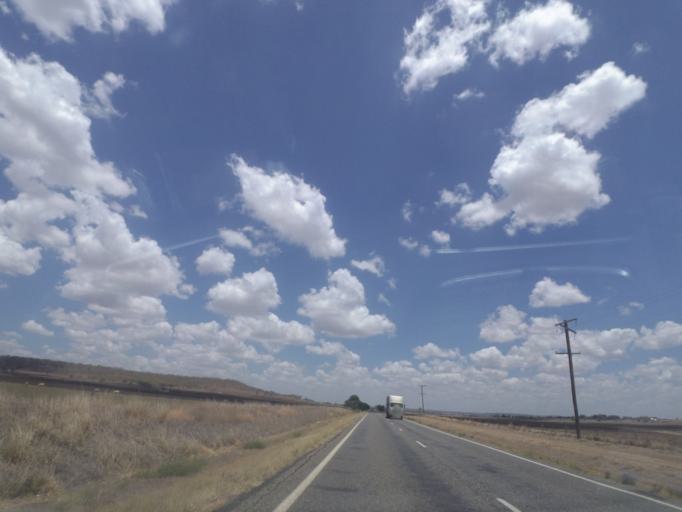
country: AU
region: Queensland
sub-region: Southern Downs
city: Warwick
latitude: -28.0050
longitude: 151.9913
